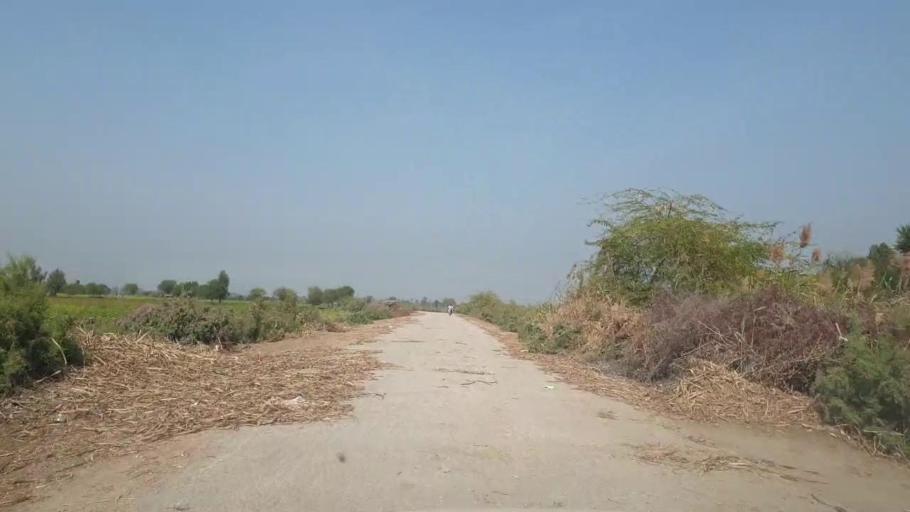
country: PK
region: Sindh
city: Mirpur Khas
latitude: 25.6715
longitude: 69.1547
